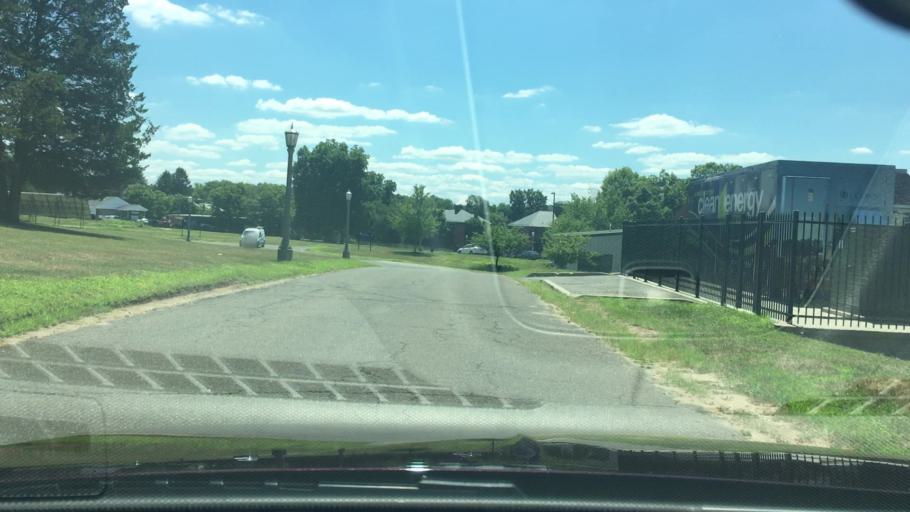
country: US
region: Connecticut
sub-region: Tolland County
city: South Coventry
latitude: 41.8101
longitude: -72.2962
